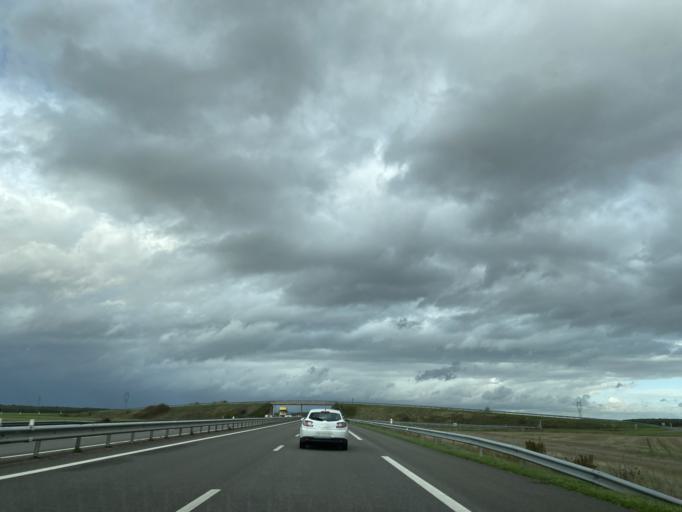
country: FR
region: Centre
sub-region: Departement du Cher
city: Levet
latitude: 46.9600
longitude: 2.4214
